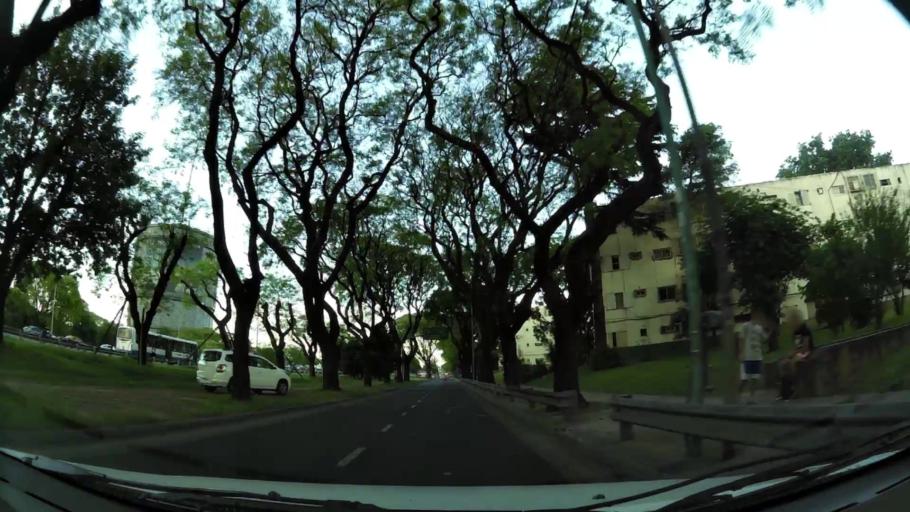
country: AR
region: Buenos Aires
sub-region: Partido de General San Martin
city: General San Martin
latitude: -34.5728
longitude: -58.5104
